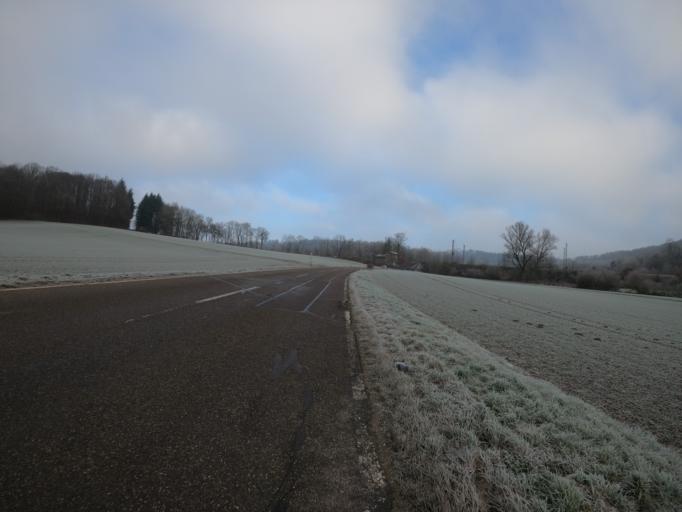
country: DE
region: Baden-Wuerttemberg
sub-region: Tuebingen Region
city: Westerstetten
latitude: 48.5260
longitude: 9.9376
